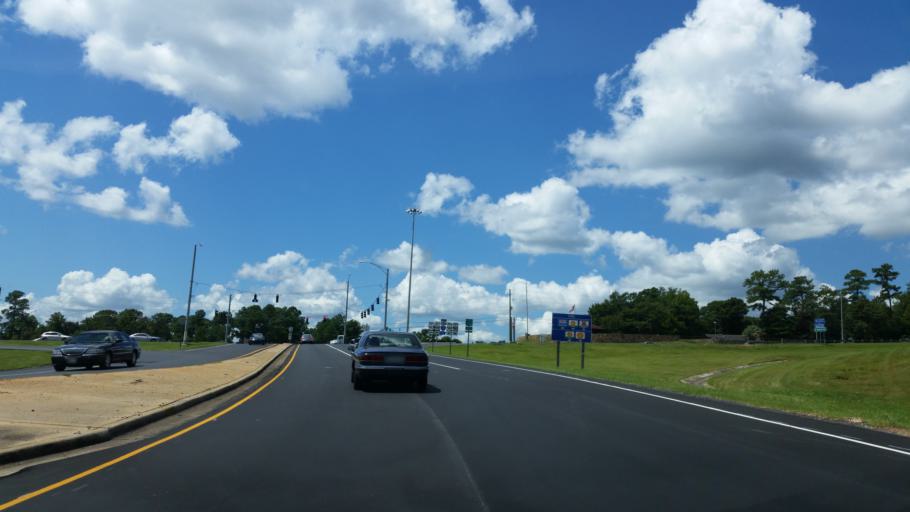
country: US
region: Alabama
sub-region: Baldwin County
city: Spanish Fort
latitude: 30.6575
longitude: -87.9100
